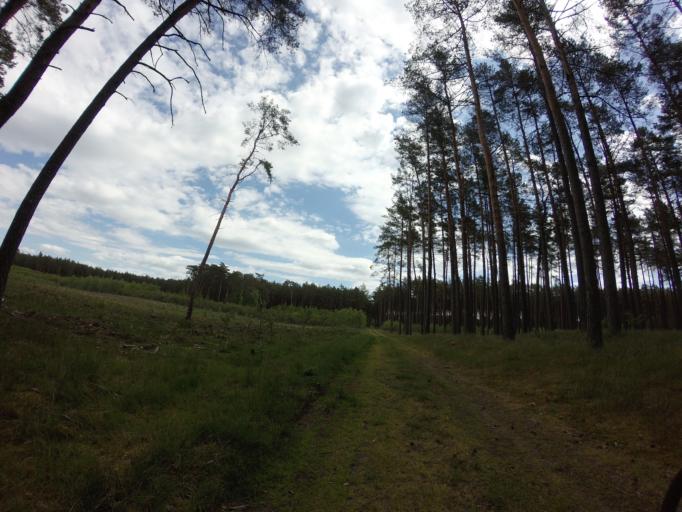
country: PL
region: West Pomeranian Voivodeship
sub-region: Powiat drawski
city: Kalisz Pomorski
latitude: 53.1599
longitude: 15.9725
